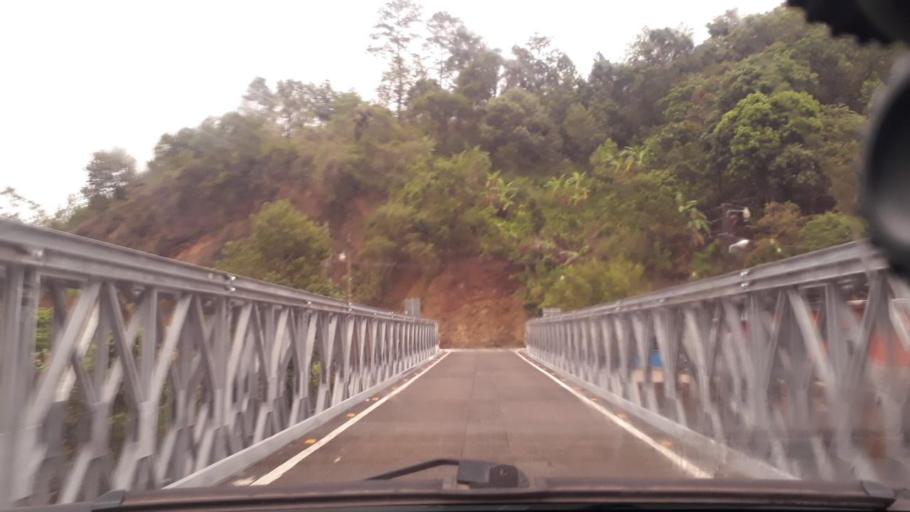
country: GT
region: Chiquimula
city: Esquipulas
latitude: 14.5313
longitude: -89.2831
